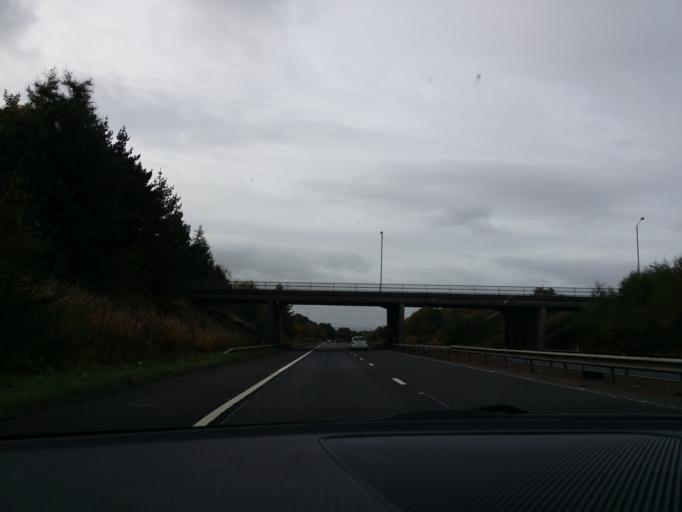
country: GB
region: Scotland
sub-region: Falkirk
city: Polmont
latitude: 55.9888
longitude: -3.6826
